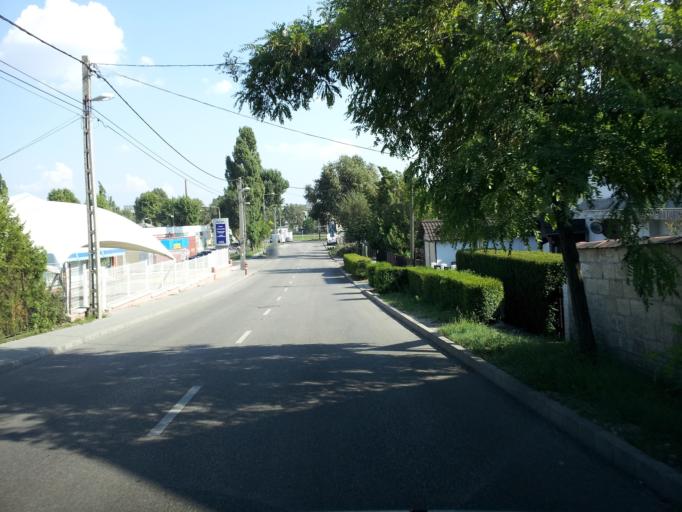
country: HU
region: Budapest
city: Budapest XXII. keruelet
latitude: 47.4127
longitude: 19.0240
